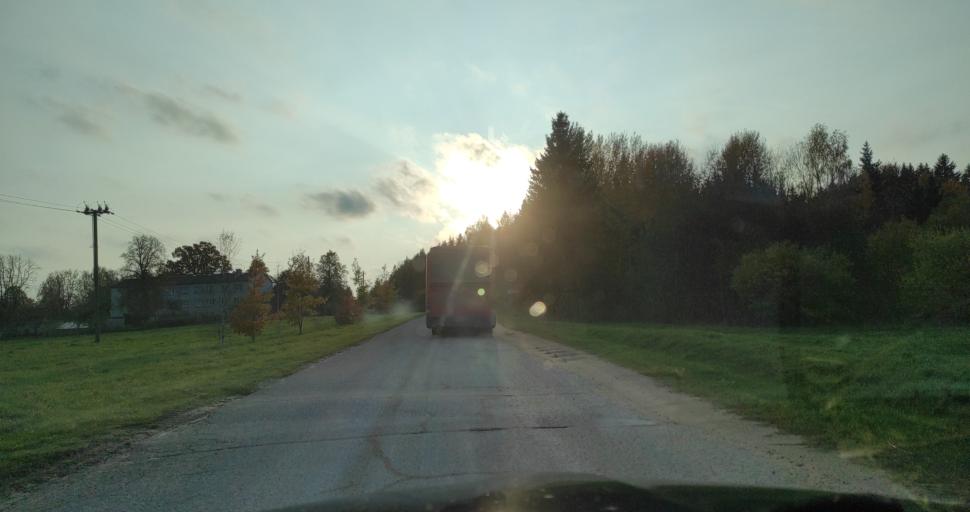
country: LV
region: Vainode
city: Vainode
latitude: 56.4378
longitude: 21.8772
